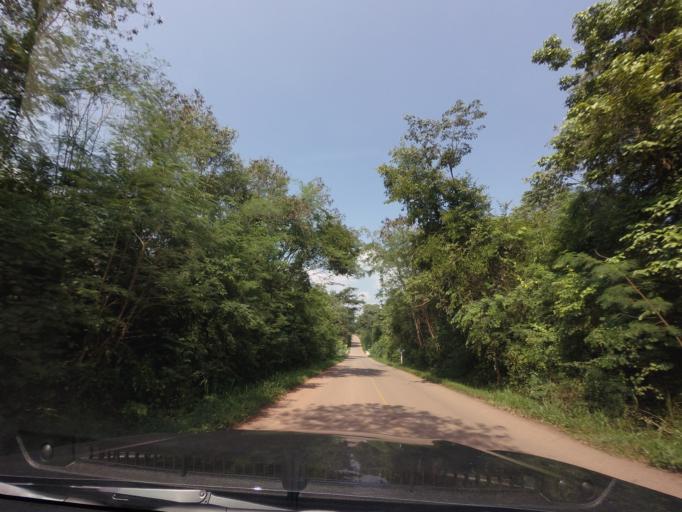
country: TH
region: Uttaradit
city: Fak Tha
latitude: 17.8700
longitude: 100.9720
